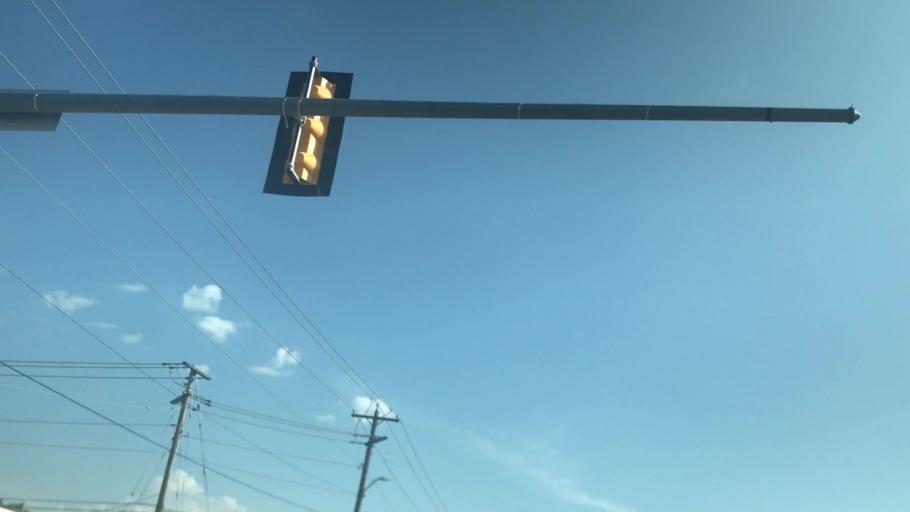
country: US
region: Wisconsin
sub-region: Brown County
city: Allouez
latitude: 44.4942
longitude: -88.0362
